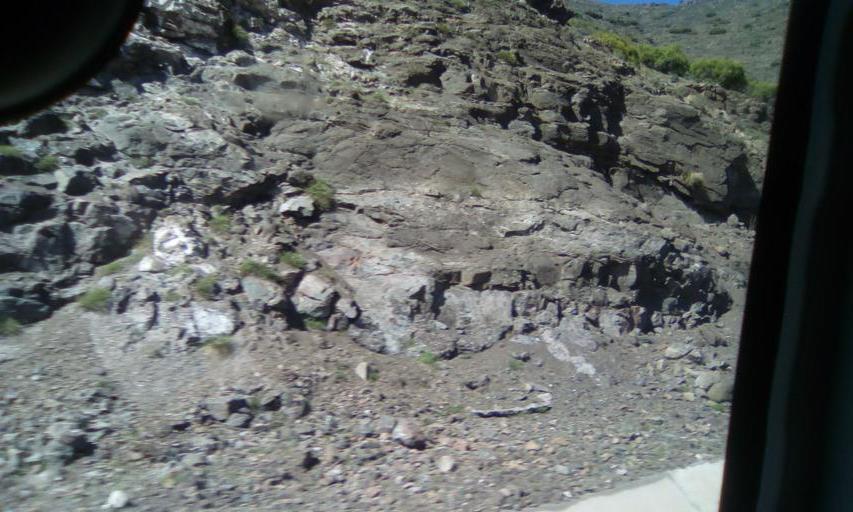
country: LS
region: Qacha's Nek
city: Qacha's Nek
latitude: -30.0101
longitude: 28.1661
